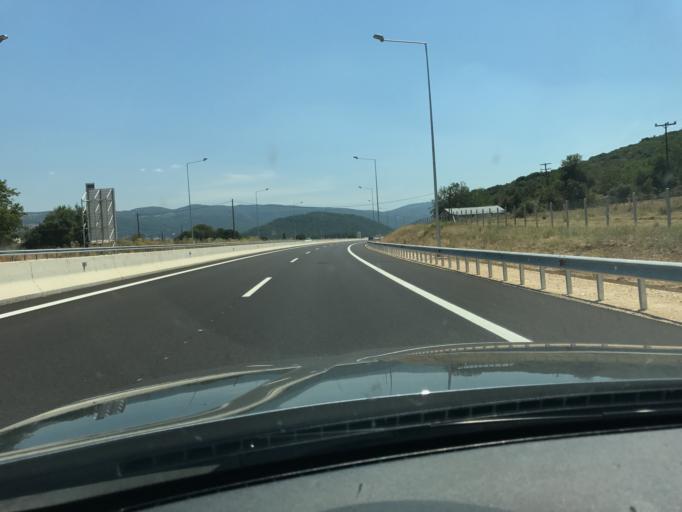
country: GR
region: Epirus
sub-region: Nomos Ioanninon
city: Agia Kyriaki
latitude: 39.5436
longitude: 20.8598
